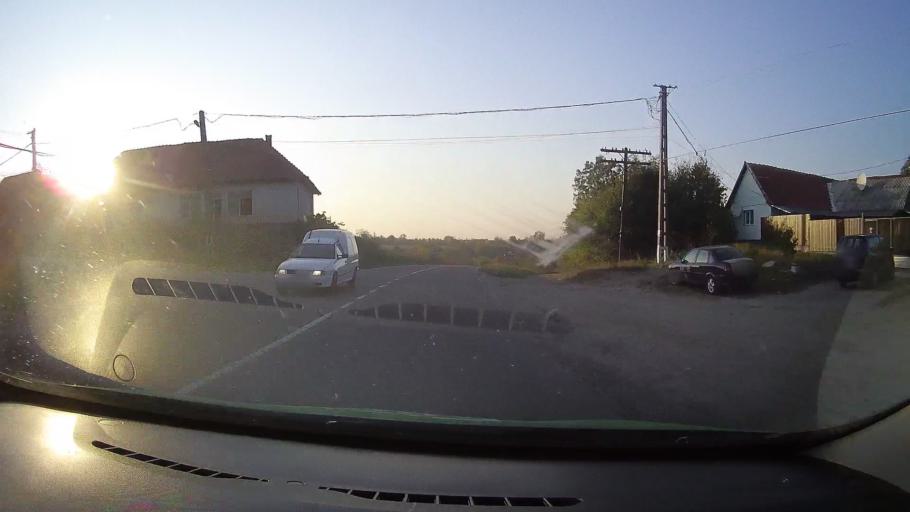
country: RO
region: Arad
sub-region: Comuna Barsa
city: Barsa
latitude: 46.3949
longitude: 22.0379
